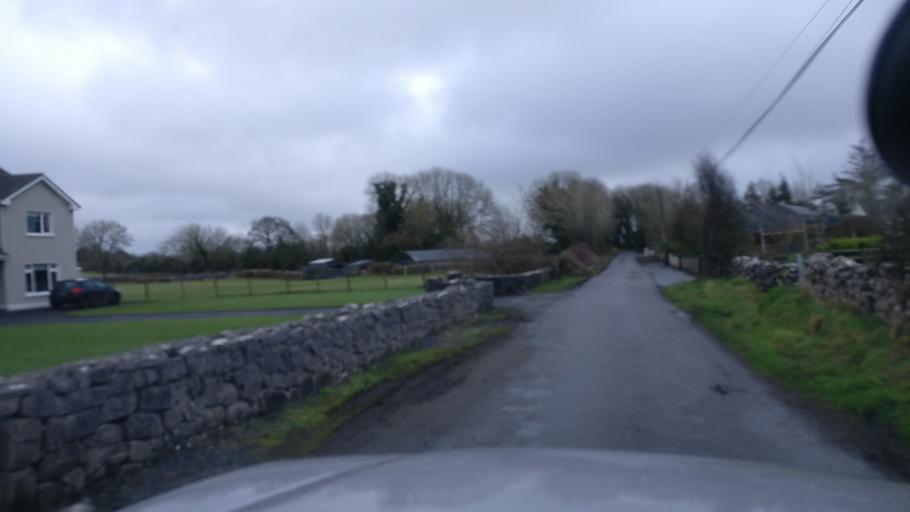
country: IE
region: Connaught
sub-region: County Galway
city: Athenry
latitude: 53.2082
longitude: -8.6811
